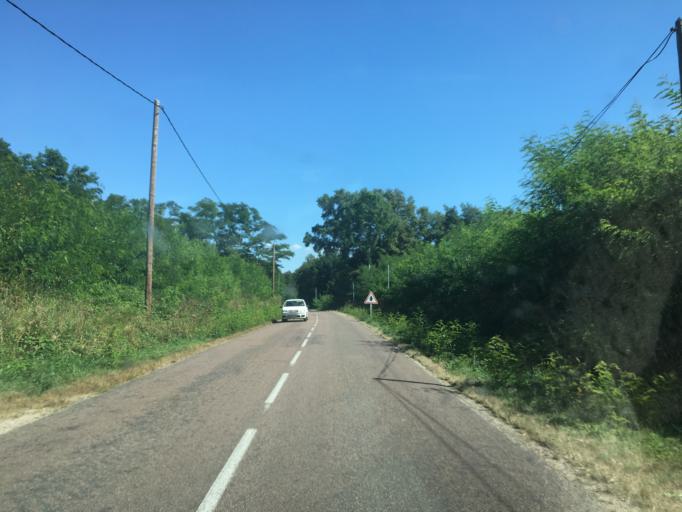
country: FR
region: Bourgogne
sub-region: Departement de l'Yonne
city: Fleury-la-Vallee
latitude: 47.8555
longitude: 3.4618
